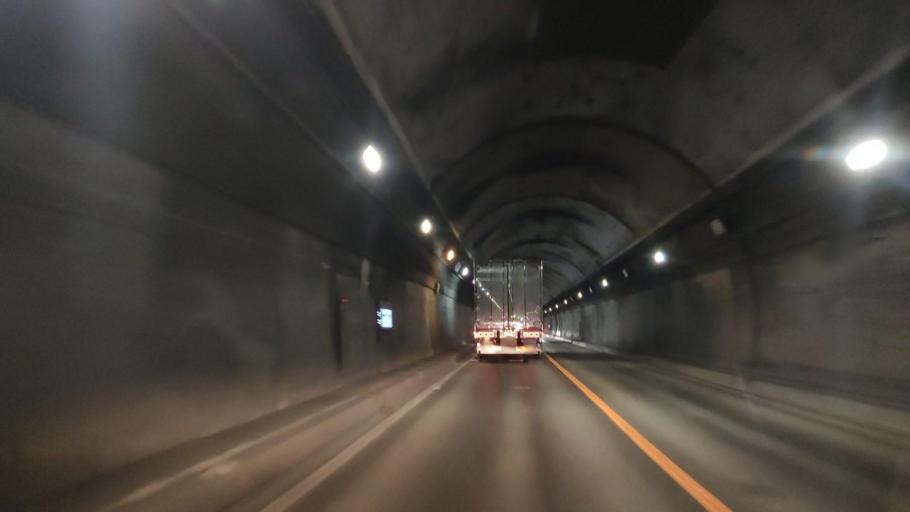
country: JP
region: Aomori
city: Aomori Shi
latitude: 40.7746
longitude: 140.9745
